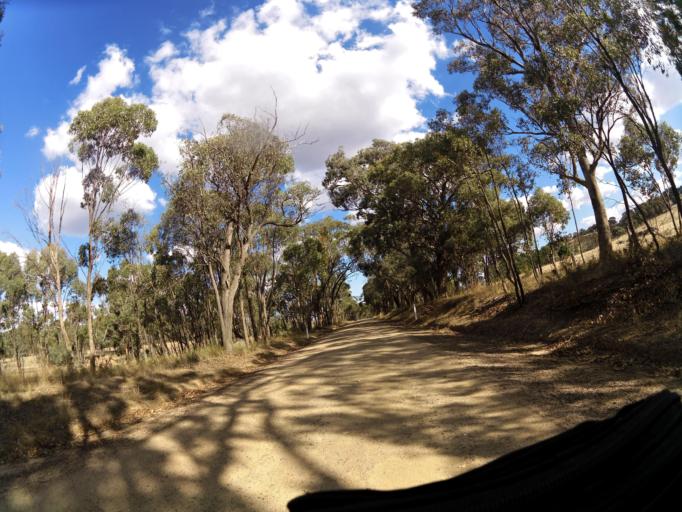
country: AU
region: Victoria
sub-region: Greater Bendigo
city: Kennington
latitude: -36.9968
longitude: 144.8126
